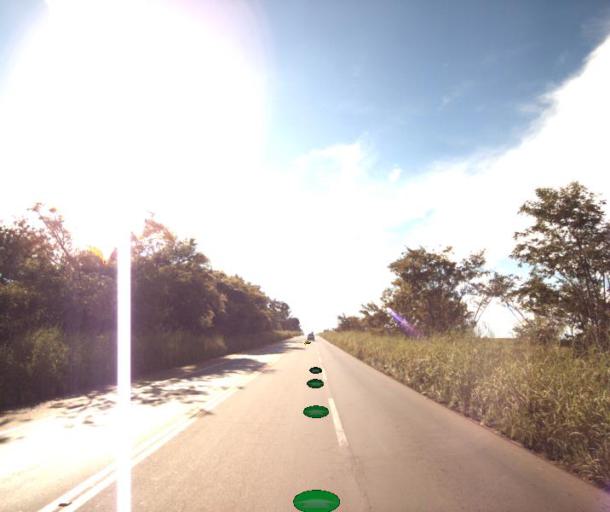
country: BR
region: Goias
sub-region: Rialma
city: Rialma
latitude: -15.4255
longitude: -49.5147
